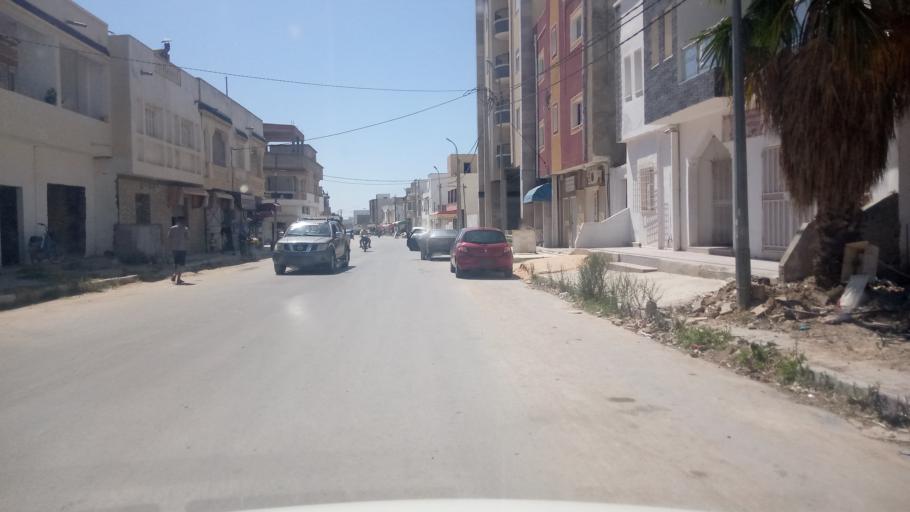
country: TN
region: Al Qayrawan
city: Sbikha
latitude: 36.1184
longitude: 10.0925
